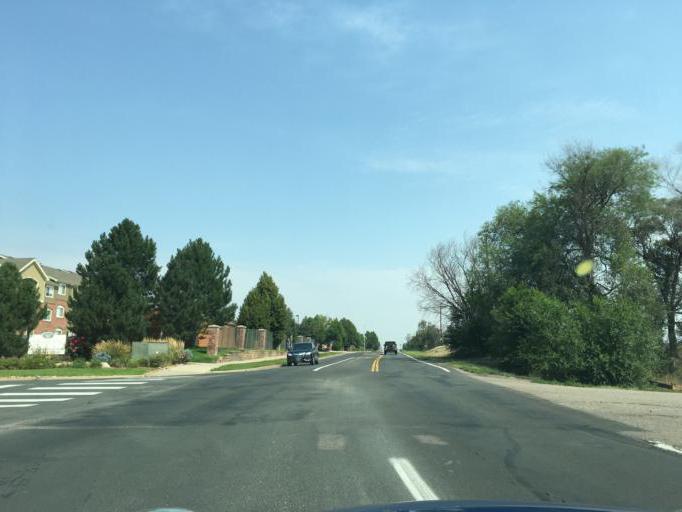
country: US
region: Colorado
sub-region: Adams County
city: Northglenn
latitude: 39.9248
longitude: -105.0154
